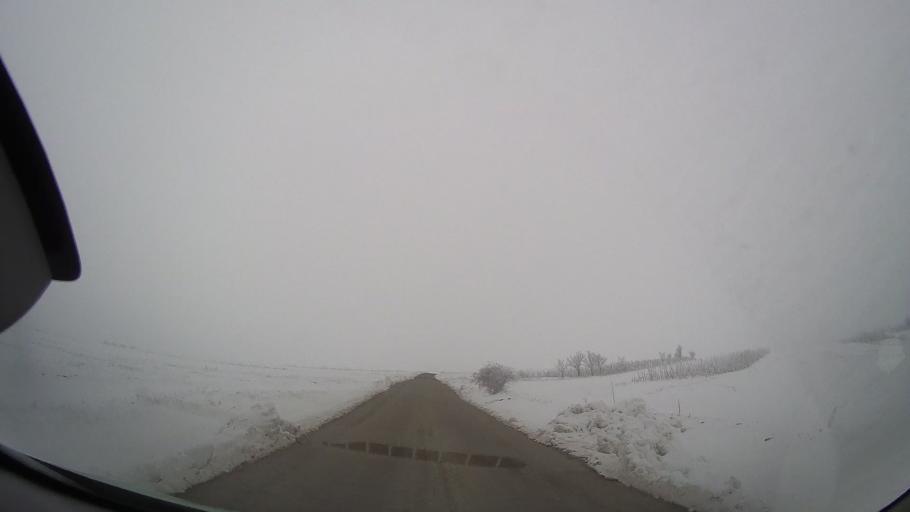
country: RO
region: Iasi
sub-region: Comuna Dagata
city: Dagata
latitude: 46.9082
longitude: 27.1971
